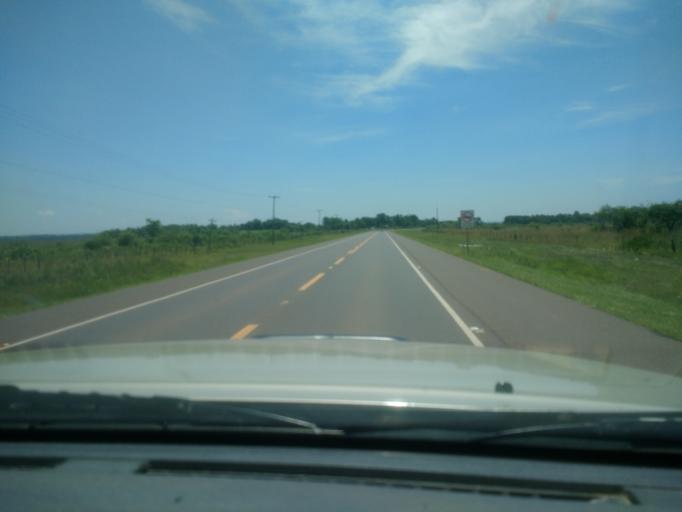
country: PY
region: San Pedro
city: Union
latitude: -24.7181
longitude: -56.5372
